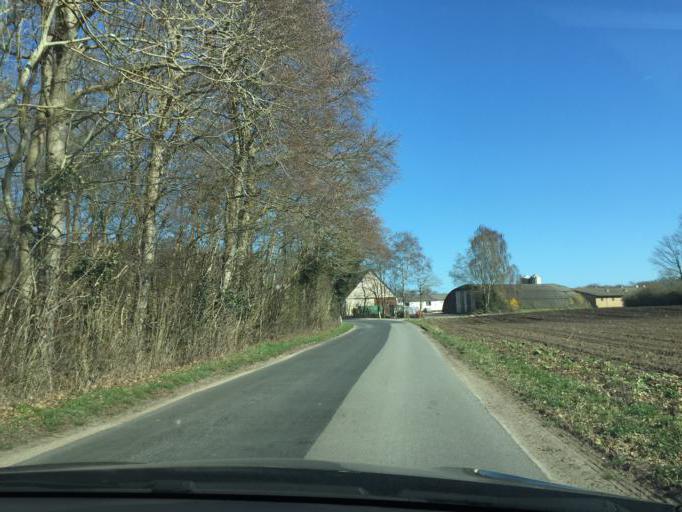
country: DK
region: South Denmark
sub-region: Kerteminde Kommune
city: Langeskov
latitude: 55.3417
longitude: 10.5653
